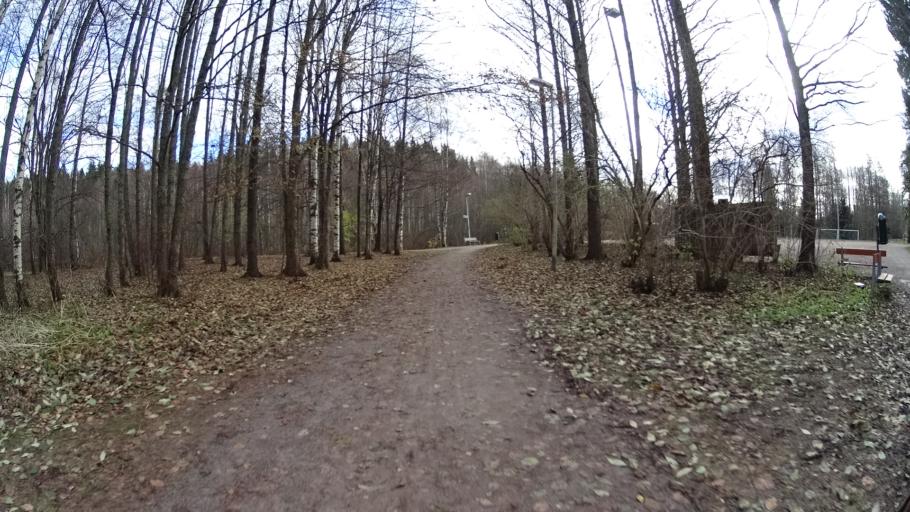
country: FI
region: Uusimaa
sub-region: Helsinki
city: Teekkarikylae
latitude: 60.2616
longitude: 24.8610
